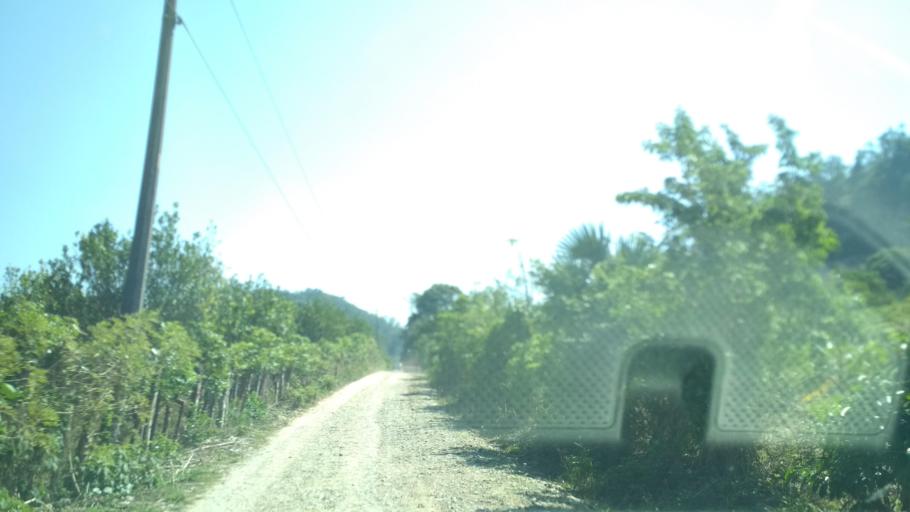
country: MX
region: Veracruz
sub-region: Papantla
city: Polutla
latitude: 20.4784
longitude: -97.2208
